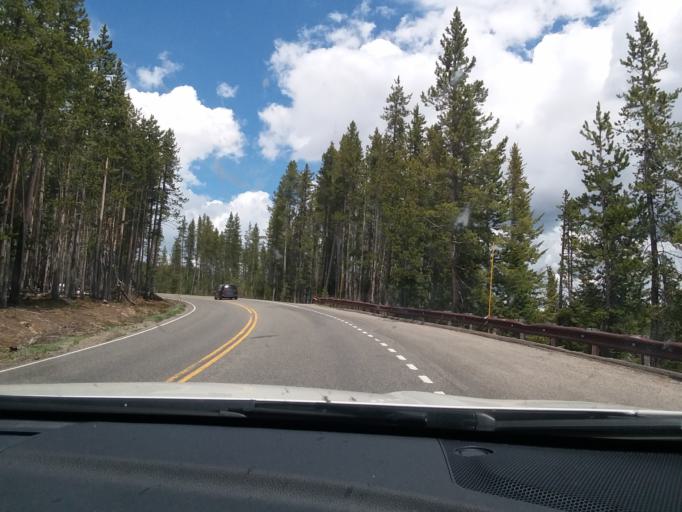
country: US
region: Montana
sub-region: Gallatin County
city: West Yellowstone
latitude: 44.1905
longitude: -110.6558
